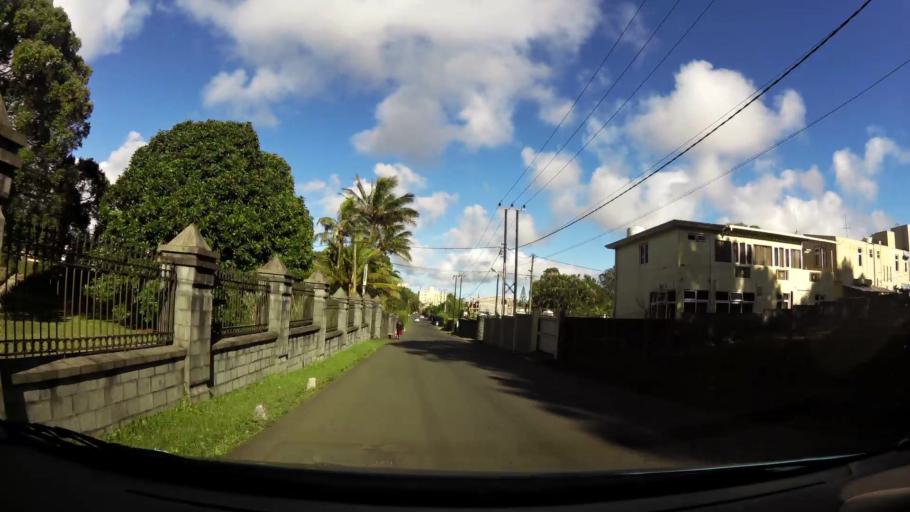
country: MU
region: Plaines Wilhems
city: Curepipe
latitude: -20.3168
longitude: 57.5334
